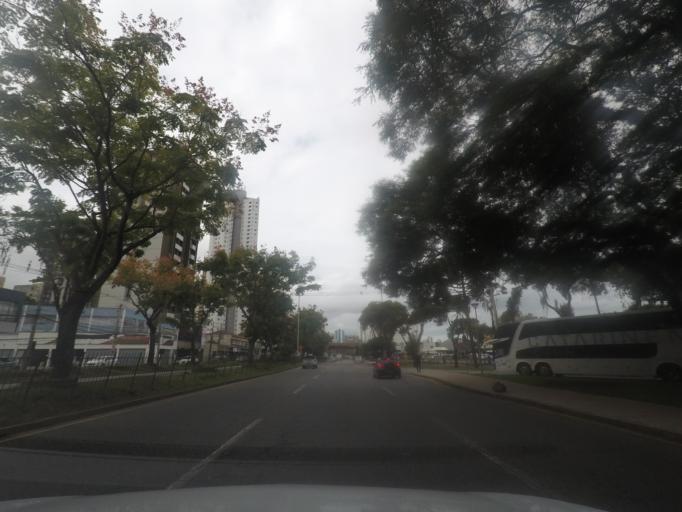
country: BR
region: Parana
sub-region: Curitiba
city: Curitiba
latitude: -25.4359
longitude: -49.2563
